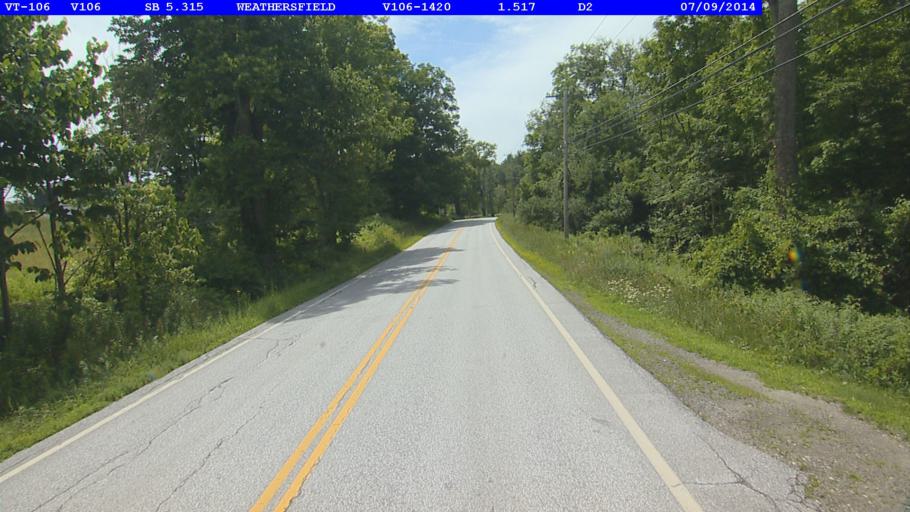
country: US
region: Vermont
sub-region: Windsor County
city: Springfield
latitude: 43.3640
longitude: -72.5183
